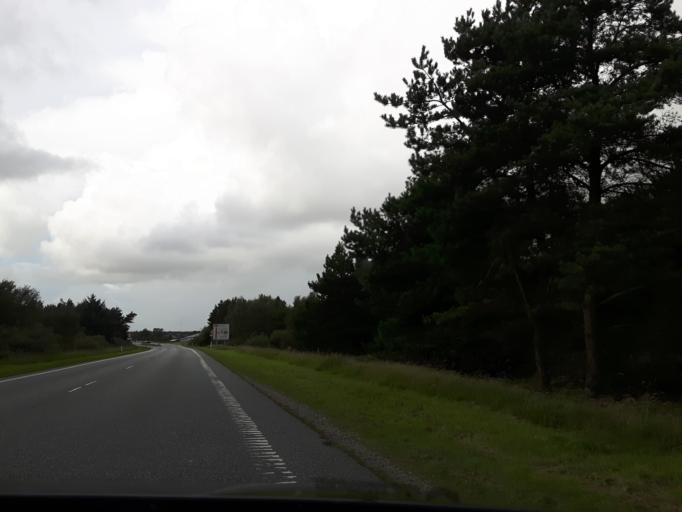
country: DK
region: North Denmark
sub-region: Thisted Kommune
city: Thisted
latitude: 57.0318
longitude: 8.8677
